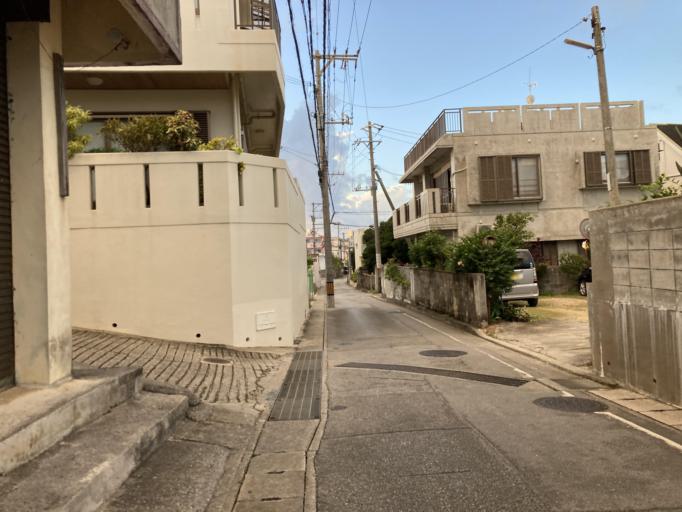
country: JP
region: Okinawa
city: Naha-shi
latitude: 26.2248
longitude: 127.7220
